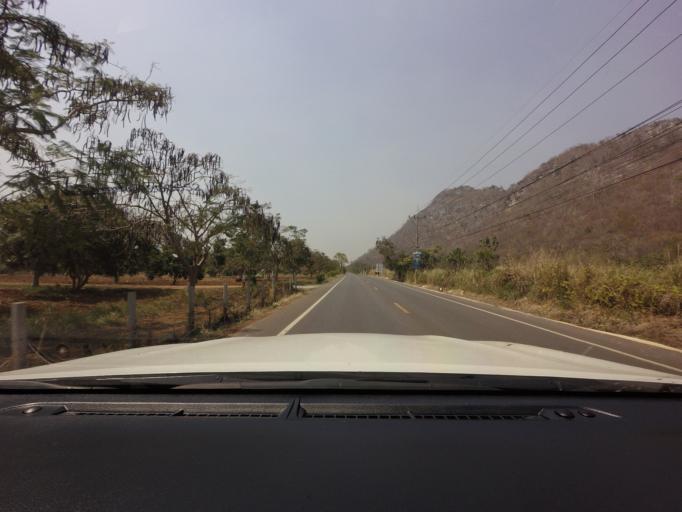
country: TH
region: Sara Buri
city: Muak Lek
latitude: 14.5533
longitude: 101.3186
